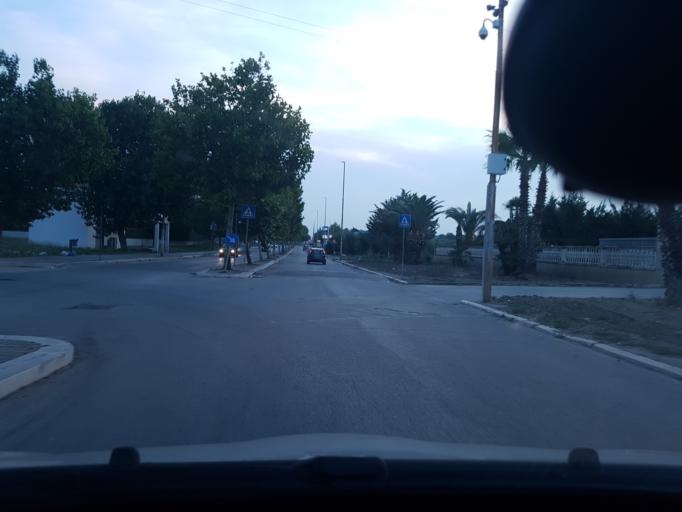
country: IT
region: Apulia
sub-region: Provincia di Foggia
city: Cerignola
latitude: 41.2634
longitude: 15.8770
